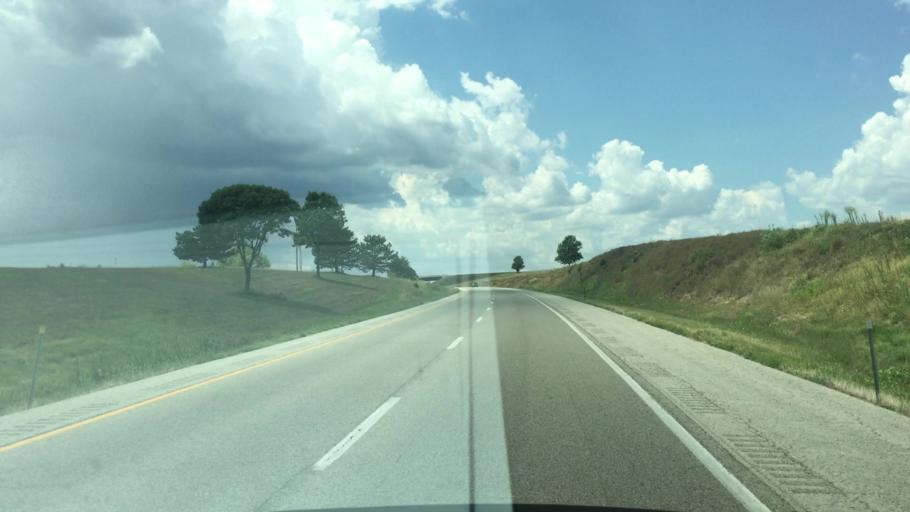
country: US
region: Kansas
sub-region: Shawnee County
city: Topeka
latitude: 39.0318
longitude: -95.6009
